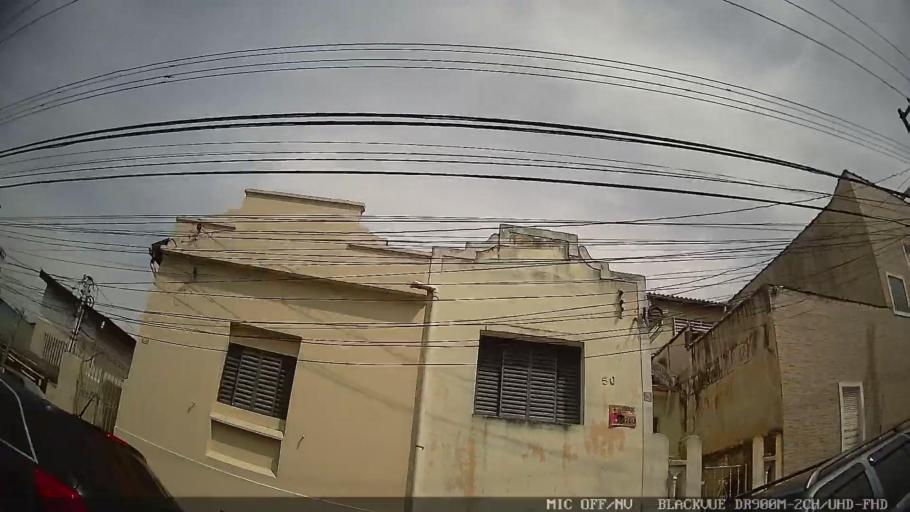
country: BR
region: Sao Paulo
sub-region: Guarulhos
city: Guarulhos
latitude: -23.5305
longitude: -46.5482
